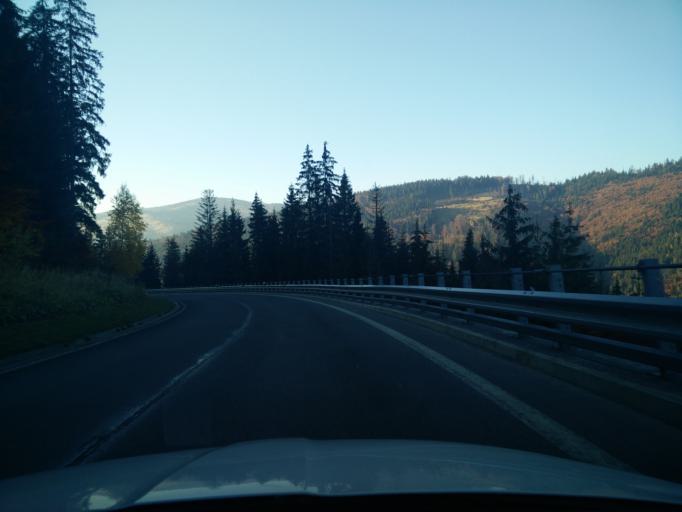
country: SK
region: Zilinsky
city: Oravska Lesna
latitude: 49.3747
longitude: 19.0905
